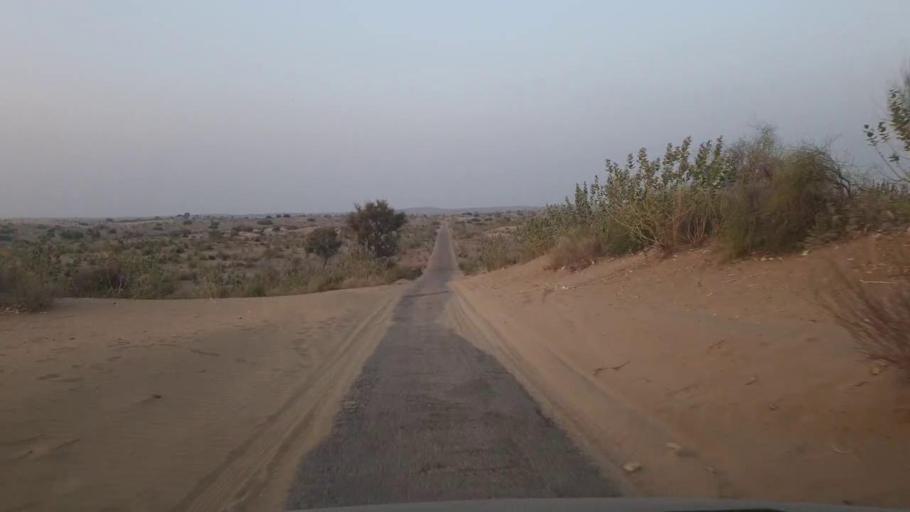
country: PK
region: Sindh
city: Umarkot
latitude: 25.2807
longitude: 70.0766
